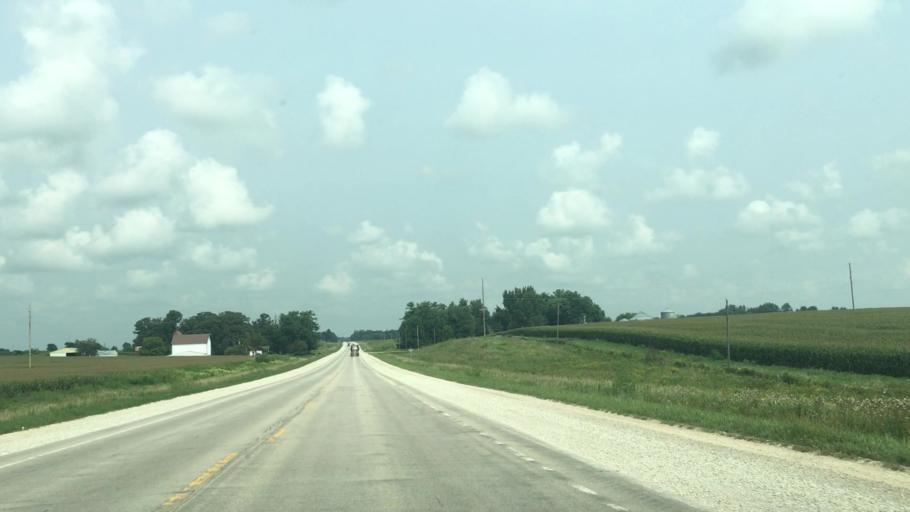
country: US
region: Minnesota
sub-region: Fillmore County
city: Harmony
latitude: 43.4772
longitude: -91.8702
